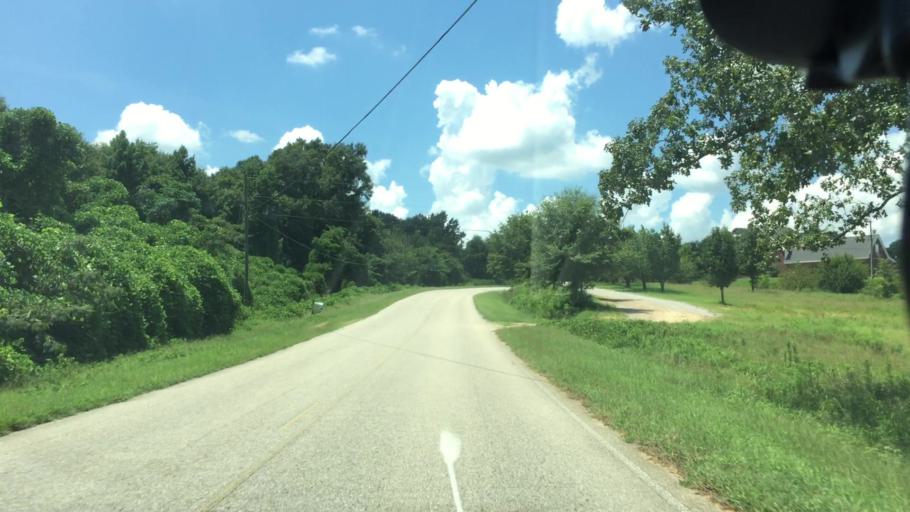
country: US
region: Alabama
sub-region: Pike County
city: Troy
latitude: 31.7506
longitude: -85.9811
